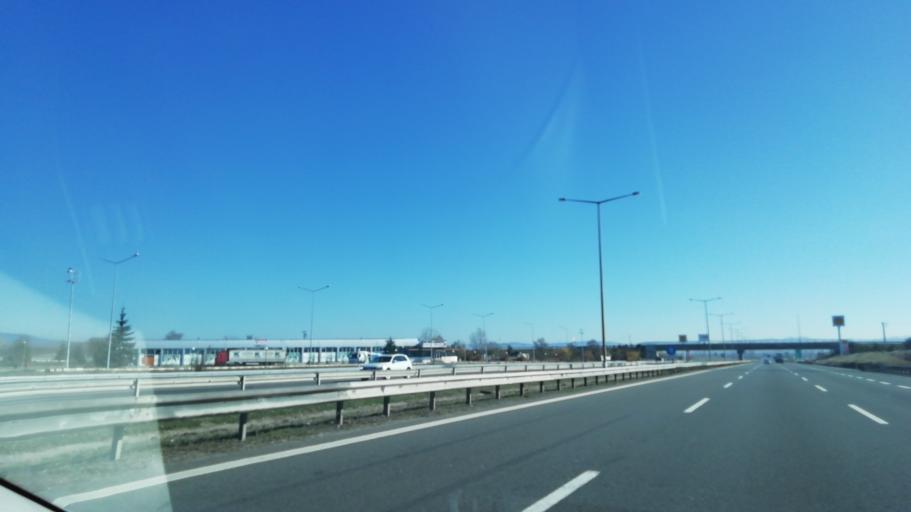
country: TR
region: Bolu
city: Dortdivan
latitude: 40.7522
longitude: 32.0773
